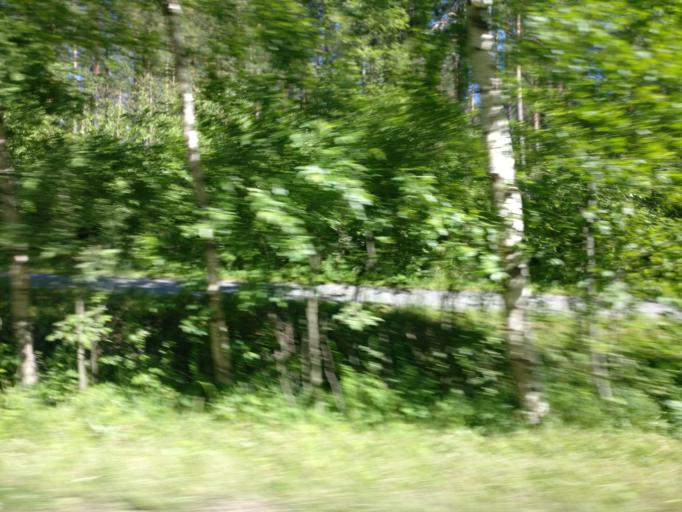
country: FI
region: Southern Savonia
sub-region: Savonlinna
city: Rantasalmi
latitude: 62.0760
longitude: 28.3035
